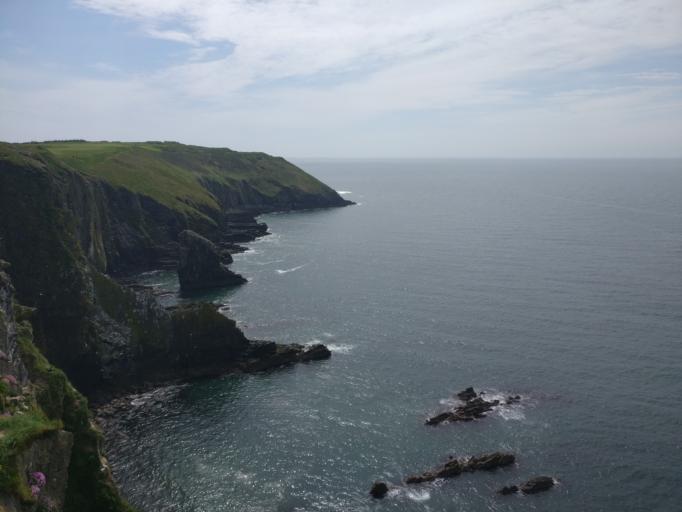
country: IE
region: Munster
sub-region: County Cork
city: Kinsale
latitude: 51.6180
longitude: -8.5426
